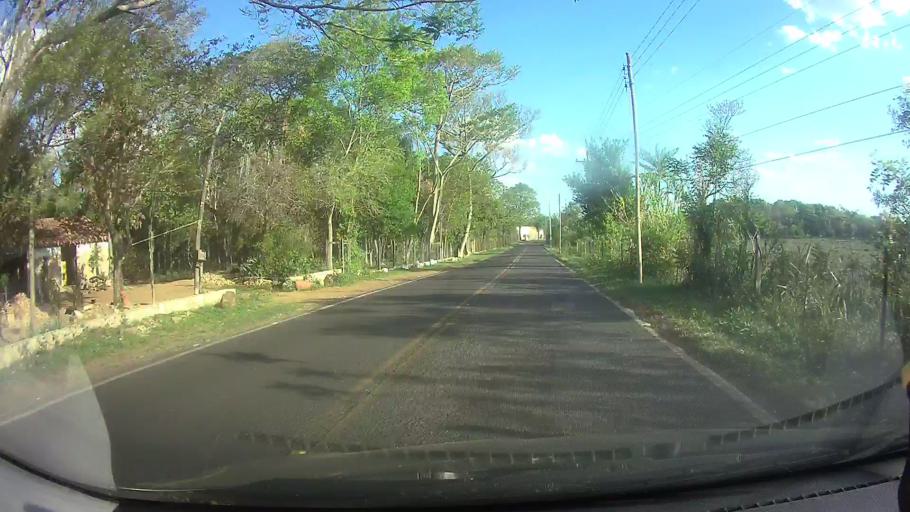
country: PY
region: Cordillera
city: Emboscada
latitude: -25.1856
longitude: -57.3185
